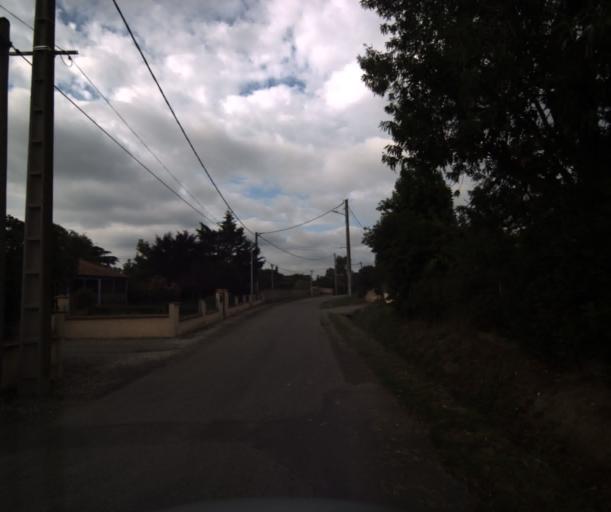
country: FR
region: Midi-Pyrenees
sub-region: Departement de la Haute-Garonne
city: Le Fauga
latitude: 43.4394
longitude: 1.2911
